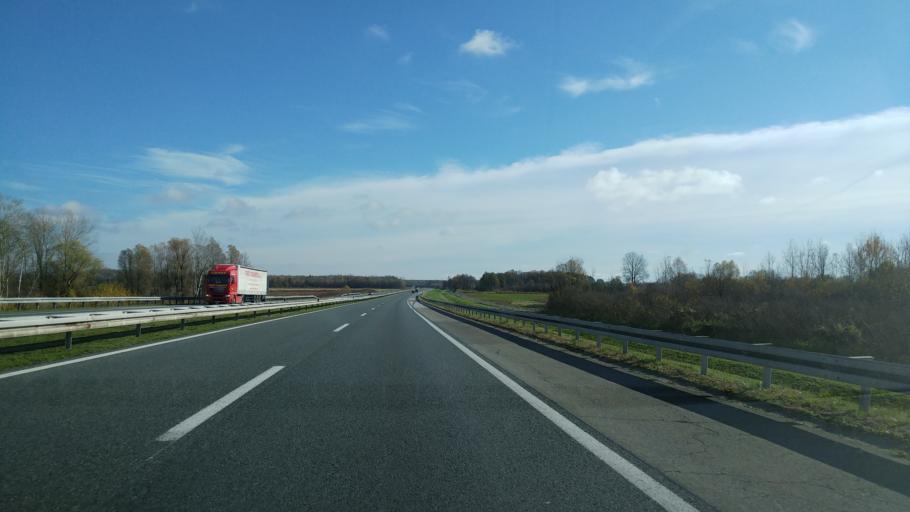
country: HR
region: Sisacko-Moslavacka
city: Novska
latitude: 45.3215
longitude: 16.9707
